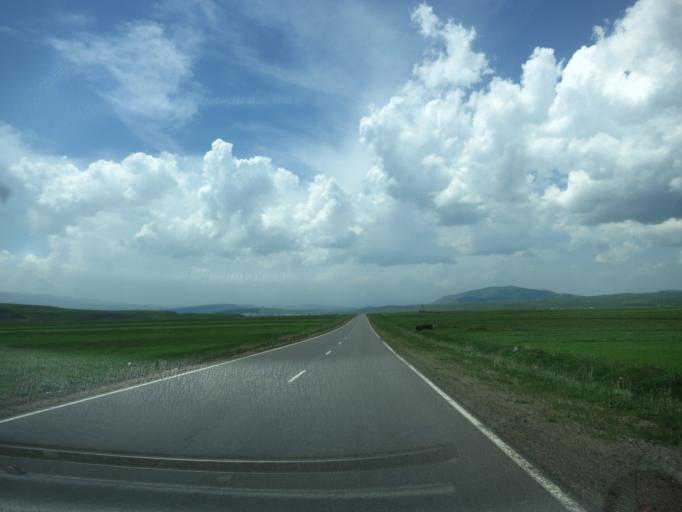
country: GE
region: Samtskhe-Javakheti
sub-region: Ninotsminda
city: Ninotsminda
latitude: 41.2934
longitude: 43.6911
